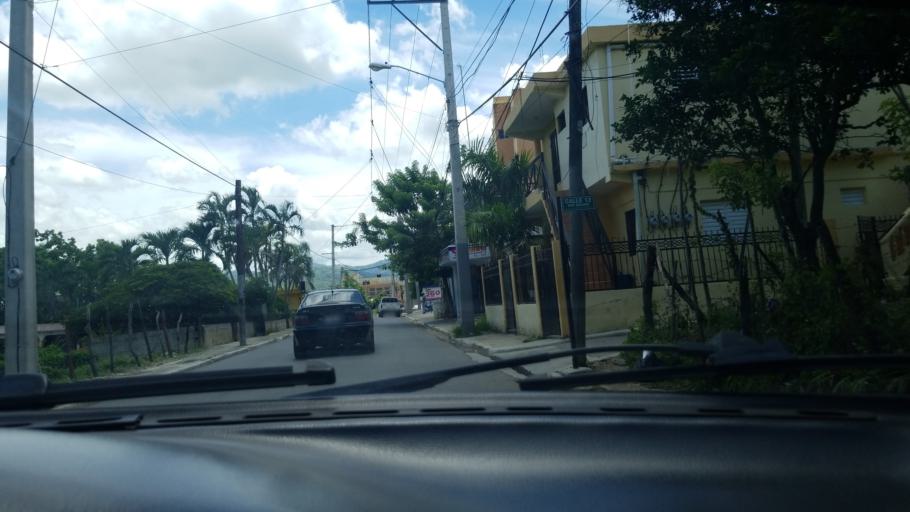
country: DO
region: Santiago
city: Santiago de los Caballeros
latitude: 19.4832
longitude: -70.6805
